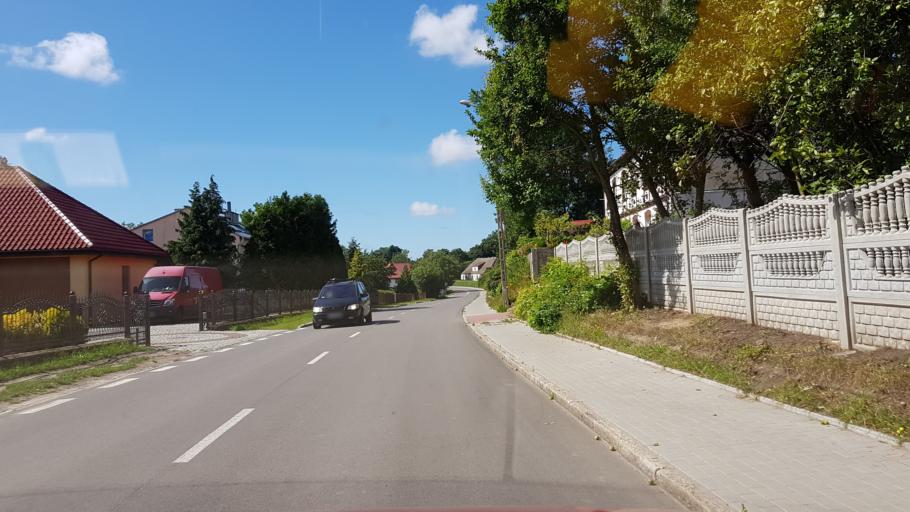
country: PL
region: West Pomeranian Voivodeship
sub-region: Powiat bialogardzki
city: Karlino
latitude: 54.1892
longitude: 15.9143
